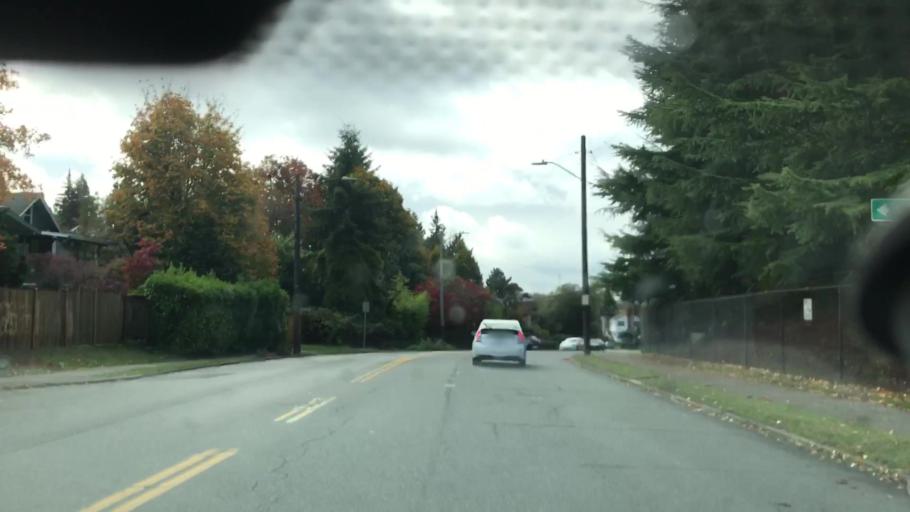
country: US
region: Washington
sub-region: King County
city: Seattle
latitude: 47.6813
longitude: -122.3117
